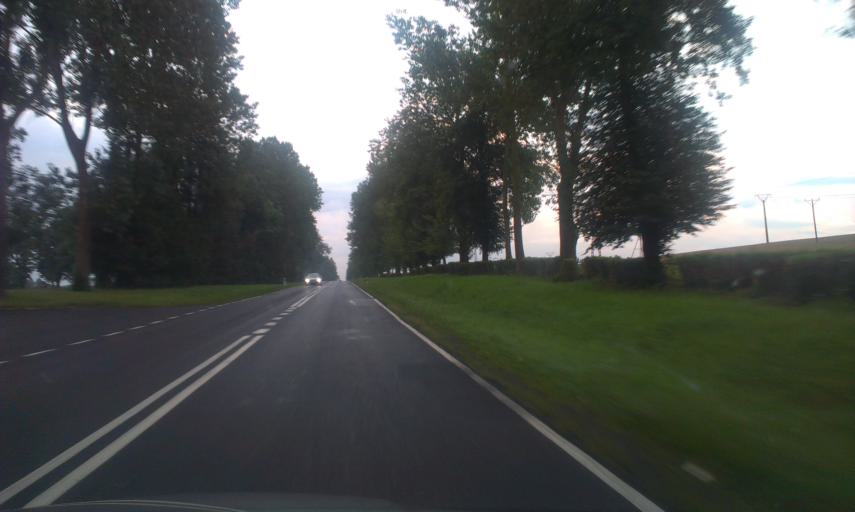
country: PL
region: West Pomeranian Voivodeship
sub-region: Powiat koszalinski
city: Sianow
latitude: 54.1431
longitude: 16.2574
